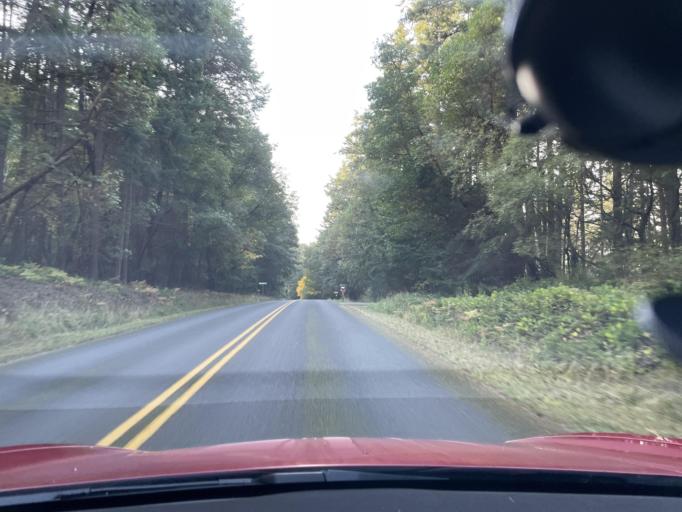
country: US
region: Washington
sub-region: San Juan County
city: Friday Harbor
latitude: 48.5451
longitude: -123.1590
